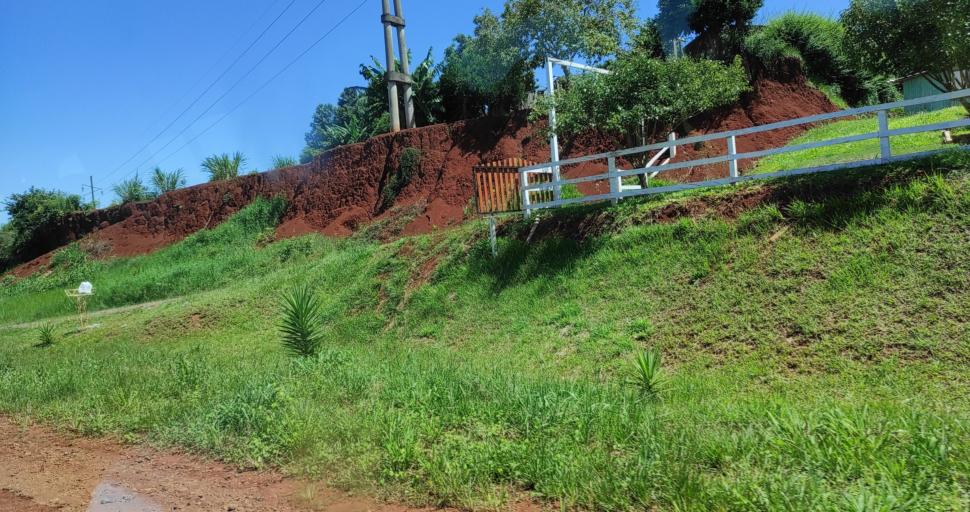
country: AR
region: Misiones
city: El Soberbio
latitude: -27.2851
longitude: -54.2227
